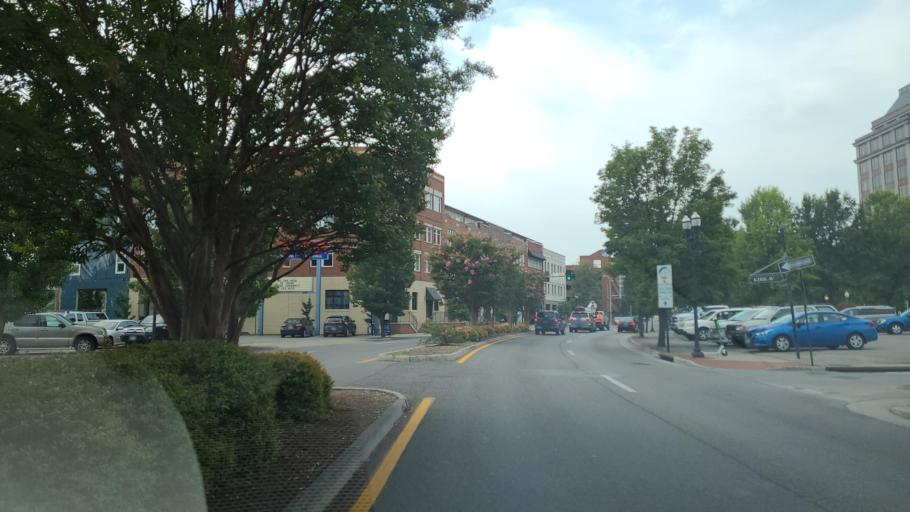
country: US
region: Virginia
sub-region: City of Roanoke
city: Roanoke
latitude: 37.2712
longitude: -79.9376
